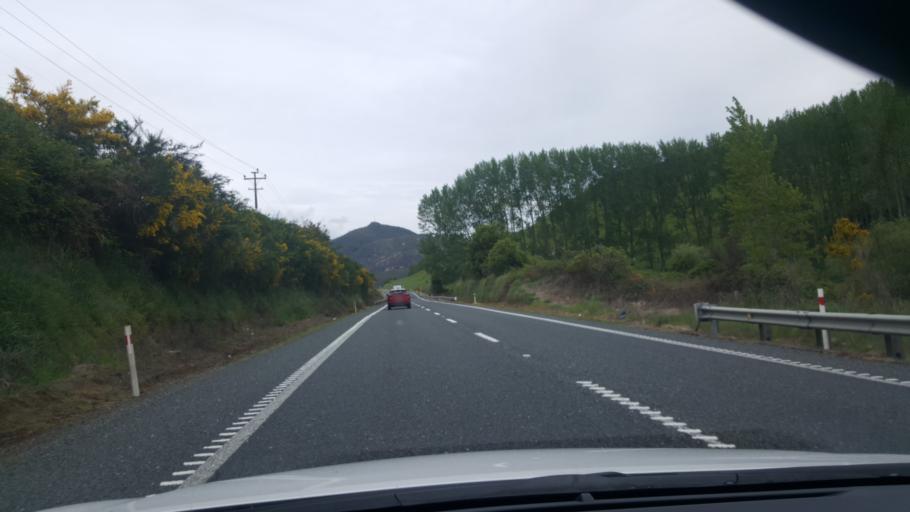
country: NZ
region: Bay of Plenty
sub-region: Rotorua District
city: Rotorua
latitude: -38.2970
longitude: 176.3599
